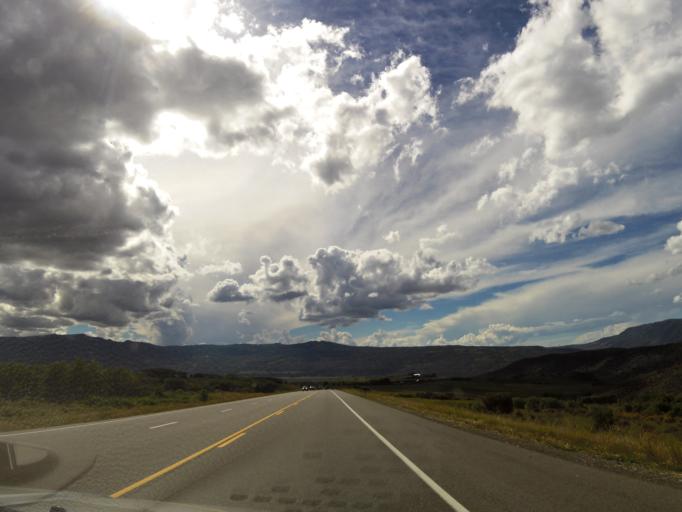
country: US
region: Colorado
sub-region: Hinsdale County
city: Lake City
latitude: 38.3960
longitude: -107.4630
